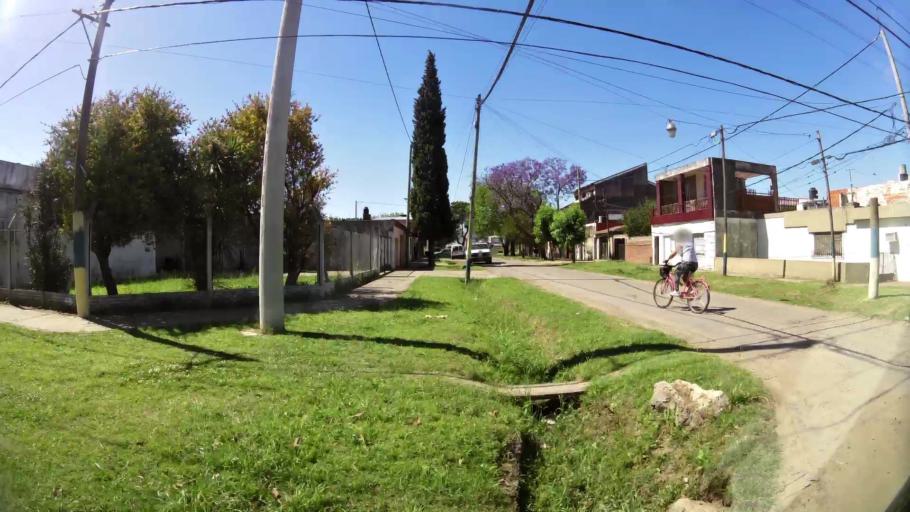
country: AR
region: Santa Fe
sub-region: Departamento de Rosario
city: Rosario
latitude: -32.9330
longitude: -60.6976
